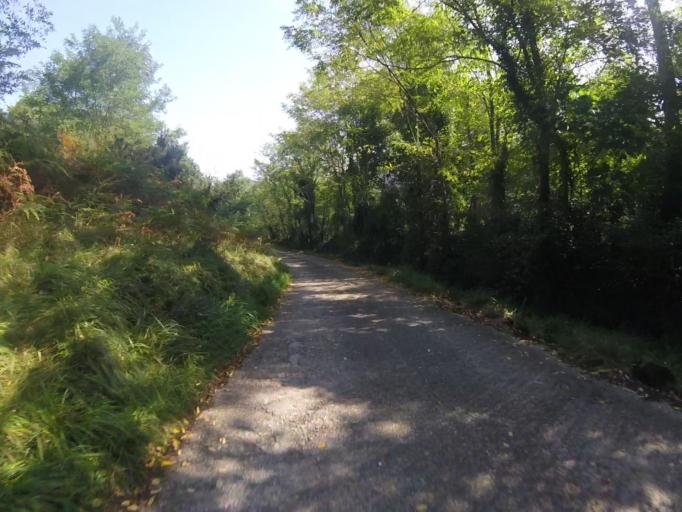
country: ES
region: Basque Country
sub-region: Provincia de Guipuzcoa
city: Irun
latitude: 43.3222
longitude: -1.7458
